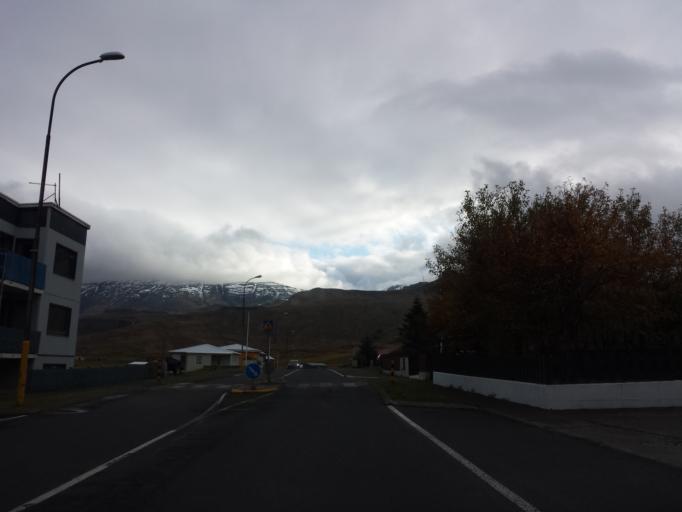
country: IS
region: West
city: Olafsvik
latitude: 64.9236
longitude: -23.2562
